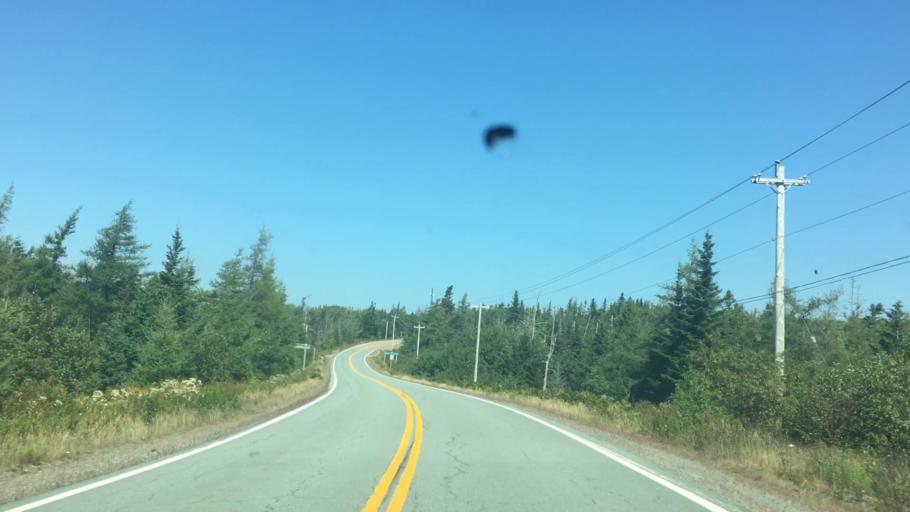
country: CA
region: Nova Scotia
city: Antigonish
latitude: 45.0219
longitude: -62.0311
